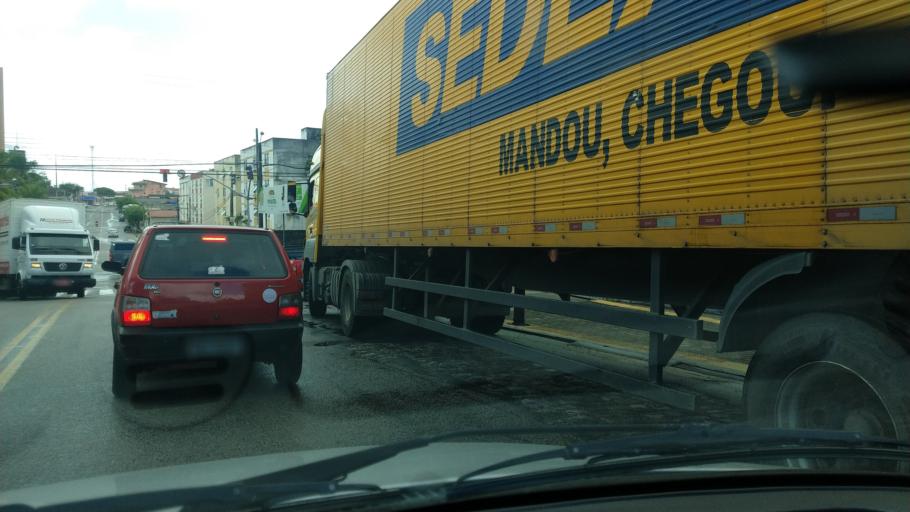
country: BR
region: Rio Grande do Norte
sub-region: Natal
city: Natal
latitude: -5.8113
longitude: -35.2186
